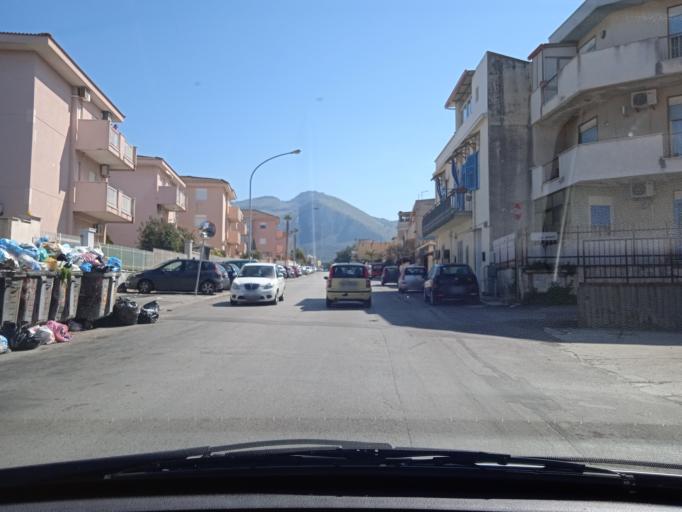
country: IT
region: Sicily
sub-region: Palermo
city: Villabate
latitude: 38.0900
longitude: 13.4325
